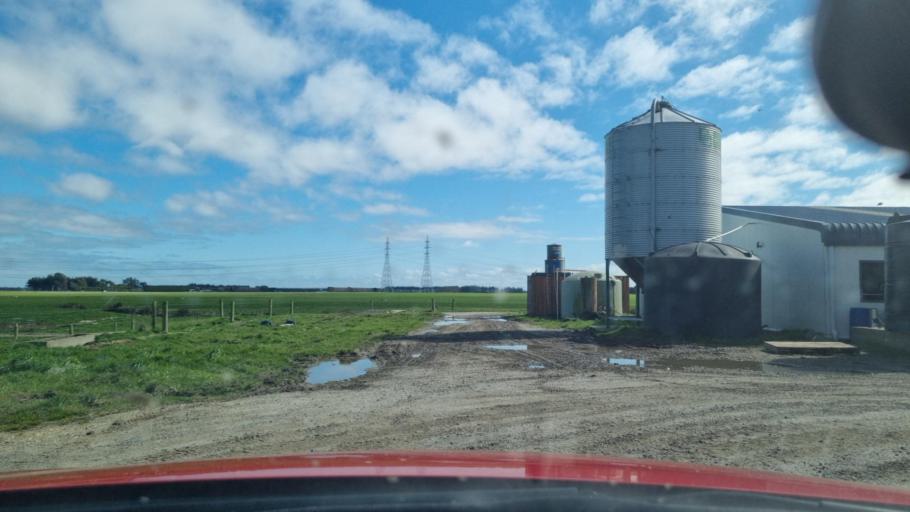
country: NZ
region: Southland
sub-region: Invercargill City
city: Invercargill
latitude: -46.5035
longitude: 168.4433
